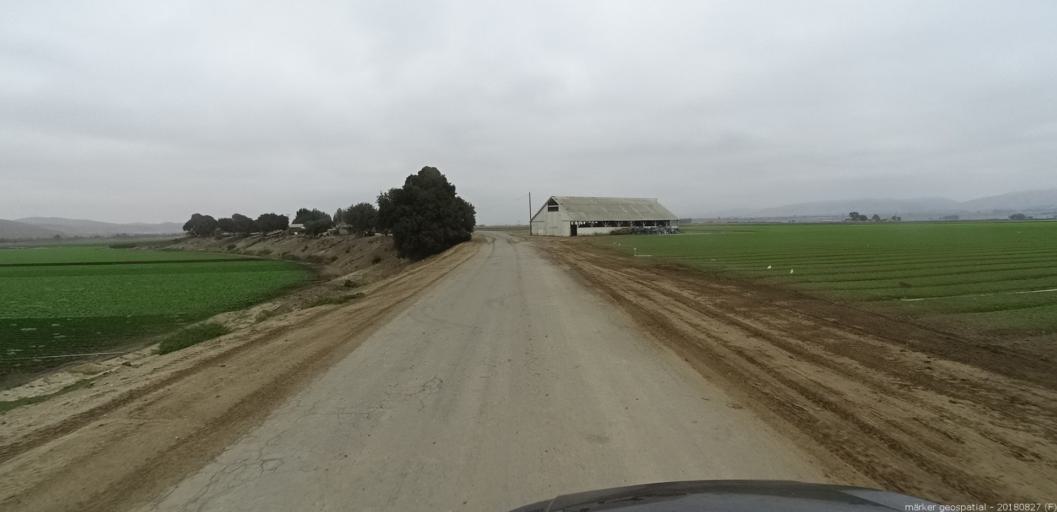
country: US
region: California
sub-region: Monterey County
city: Greenfield
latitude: 36.3267
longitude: -121.2066
